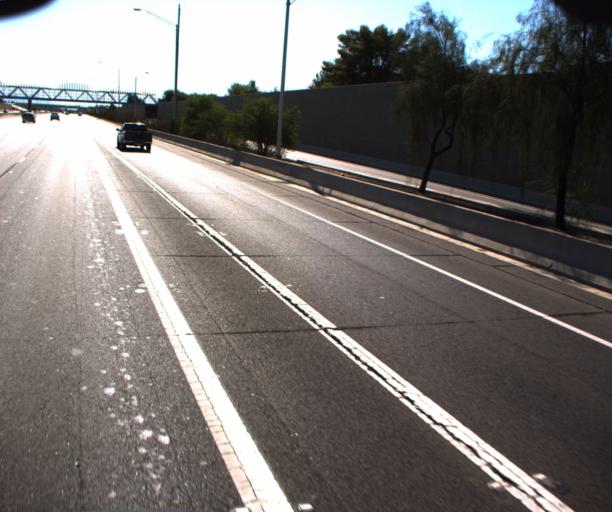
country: US
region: Arizona
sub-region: Maricopa County
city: Tempe
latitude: 33.3856
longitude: -111.9035
